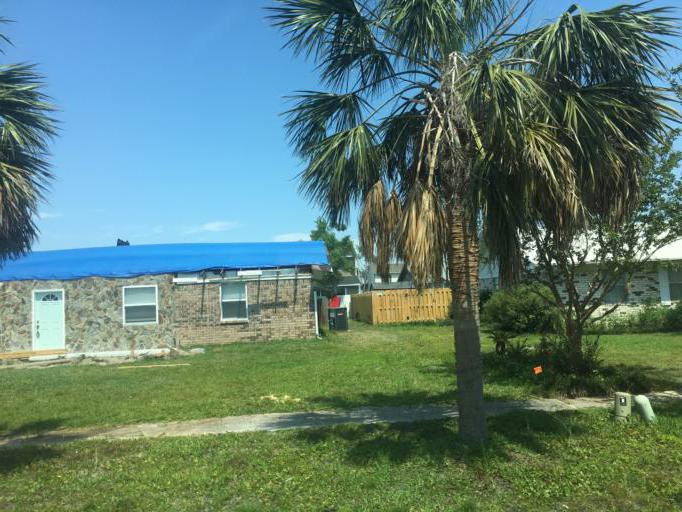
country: US
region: Florida
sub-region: Bay County
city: Lynn Haven
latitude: 30.2201
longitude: -85.6515
